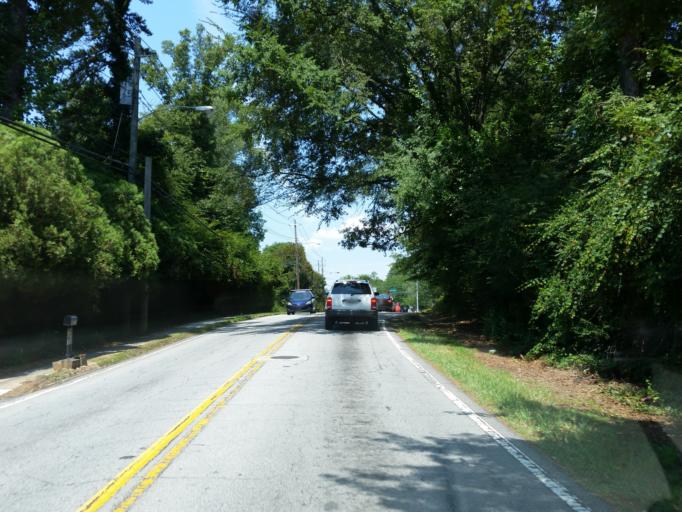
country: US
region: Georgia
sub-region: DeKalb County
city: Dunwoody
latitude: 33.9424
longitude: -84.3308
